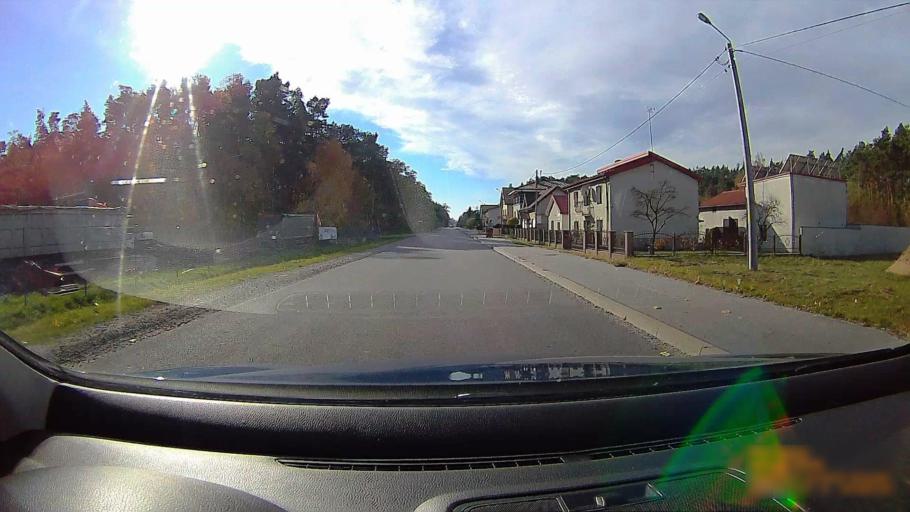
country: PL
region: Greater Poland Voivodeship
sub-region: Powiat ostrzeszowski
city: Doruchow
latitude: 51.3698
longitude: 18.0338
